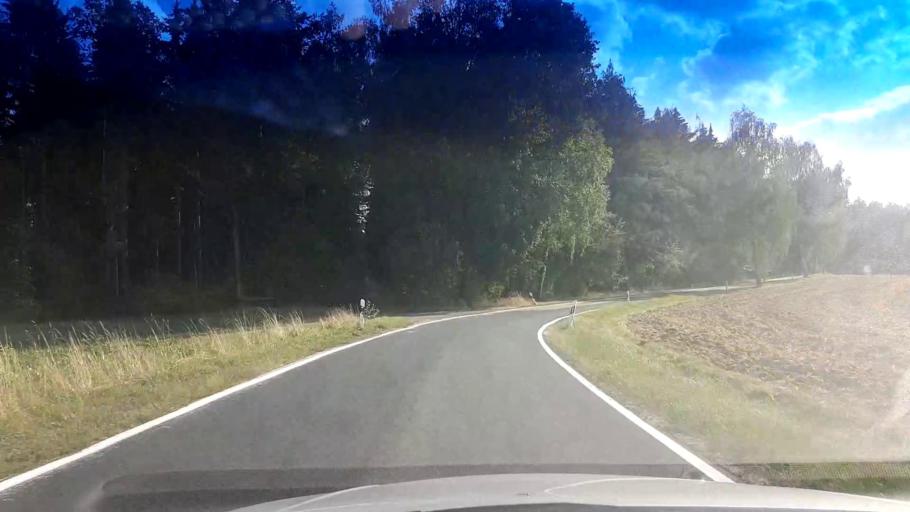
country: DE
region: Bavaria
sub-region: Upper Palatinate
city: Neualbenreuth
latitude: 49.9627
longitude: 12.4360
